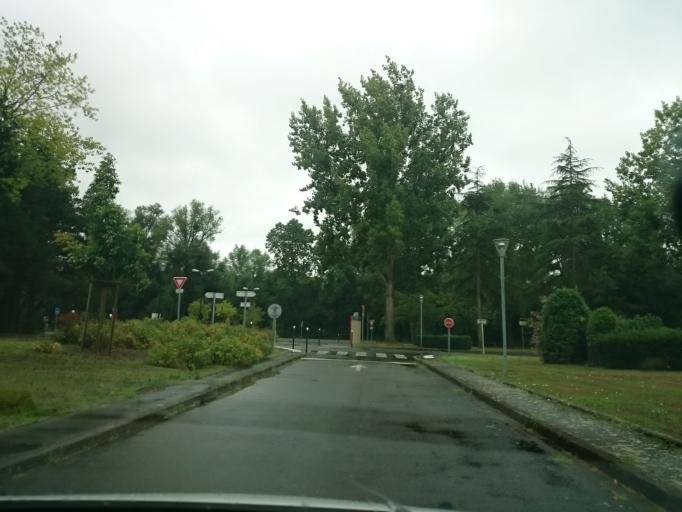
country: FR
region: Pays de la Loire
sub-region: Departement de la Loire-Atlantique
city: La Montagne
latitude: 47.1961
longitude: -1.6838
